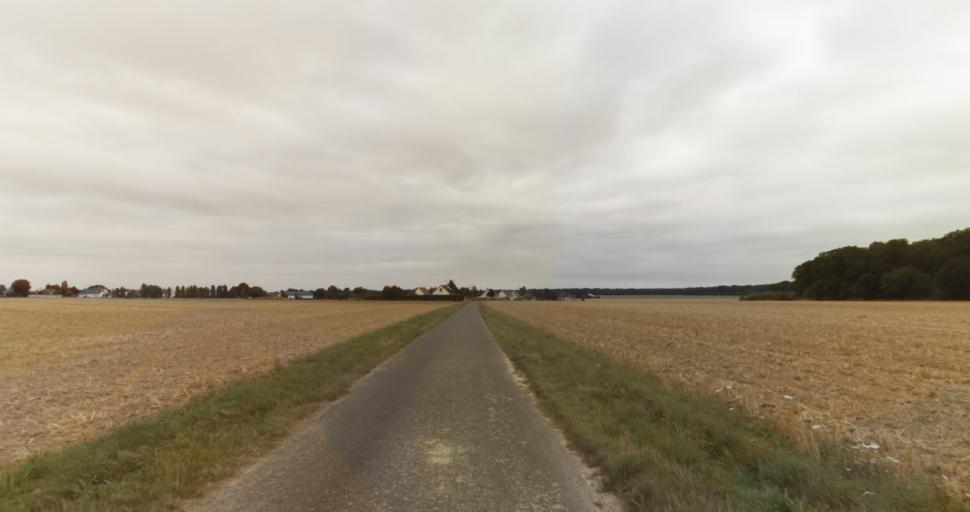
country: FR
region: Haute-Normandie
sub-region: Departement de l'Eure
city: Marcilly-sur-Eure
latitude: 48.9099
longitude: 1.3060
